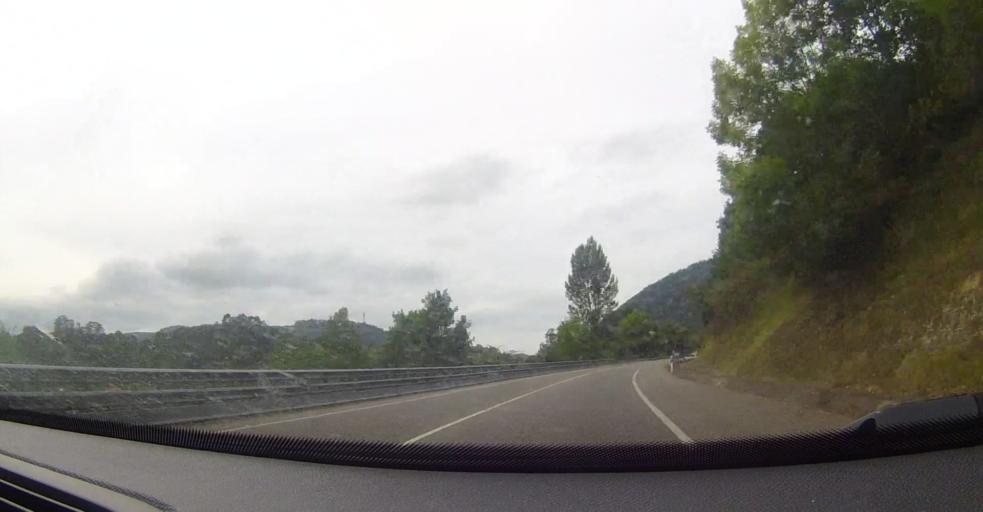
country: ES
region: Asturias
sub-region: Province of Asturias
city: Pilona
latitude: 43.3459
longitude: -5.3590
